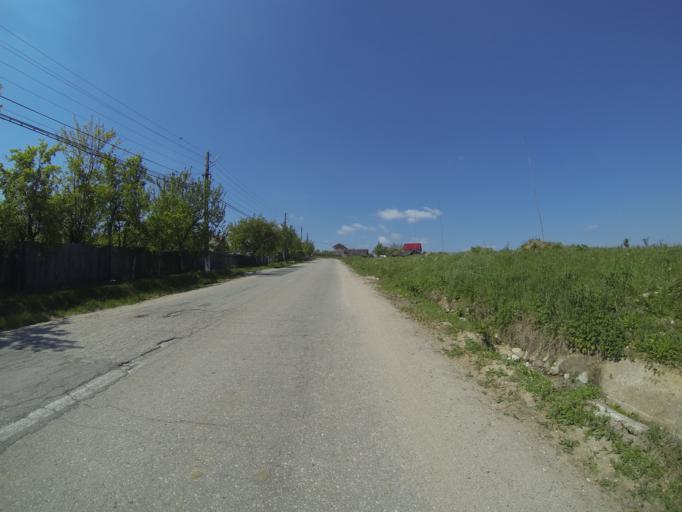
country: RO
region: Dolj
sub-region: Comuna Breasta
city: Breasta
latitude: 44.3019
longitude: 23.6616
